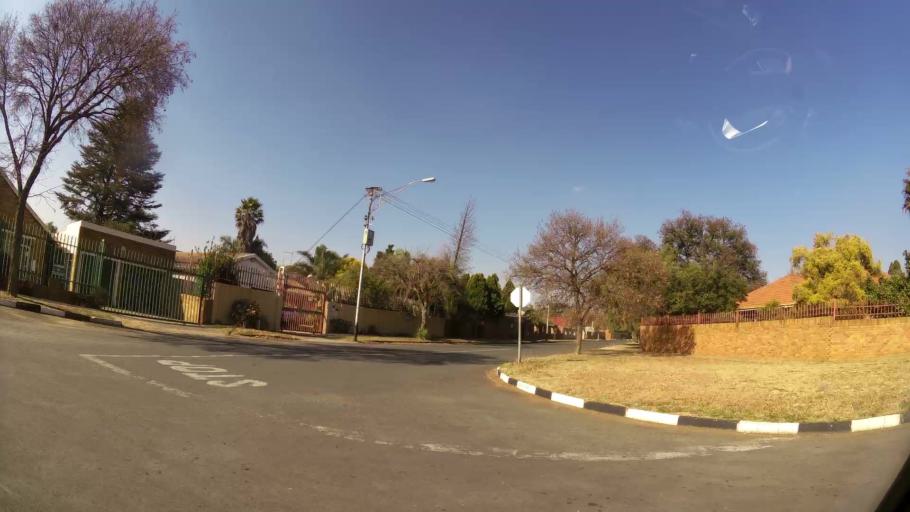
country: ZA
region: Gauteng
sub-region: City of Johannesburg Metropolitan Municipality
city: Johannesburg
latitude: -26.2539
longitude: 28.0091
